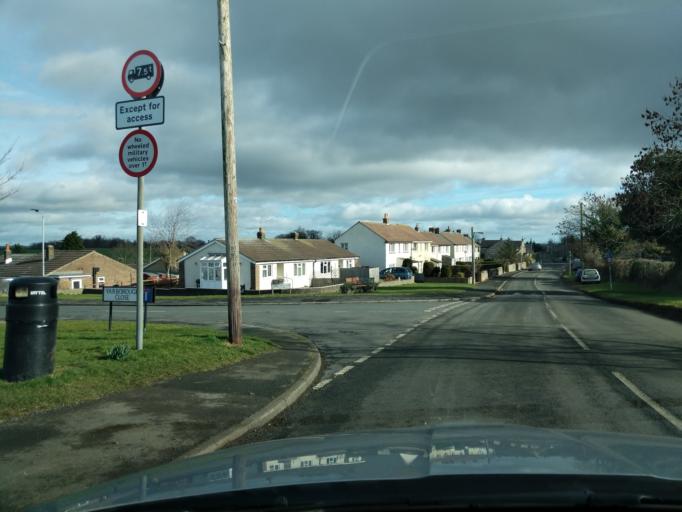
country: GB
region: England
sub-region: North Yorkshire
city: Catterick
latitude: 54.3556
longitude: -1.6740
